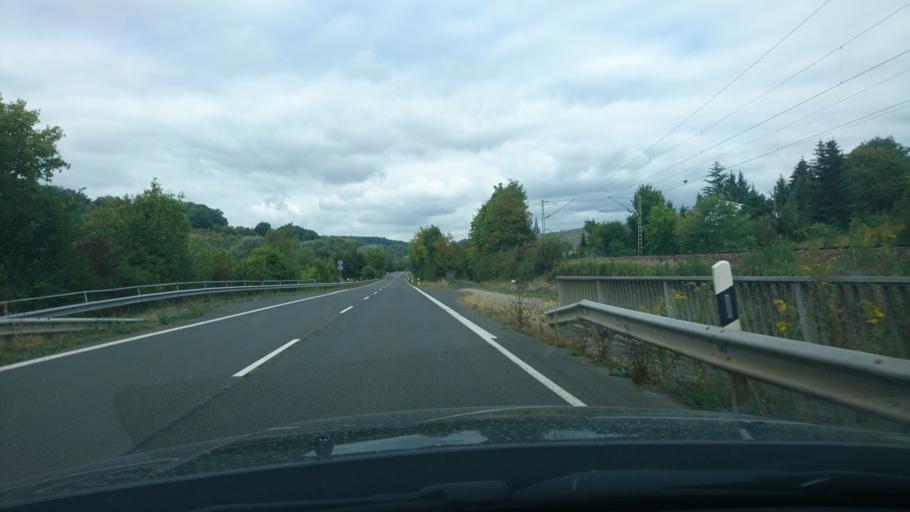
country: DE
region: Rheinland-Pfalz
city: Wiltingen
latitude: 49.6538
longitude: 6.5893
